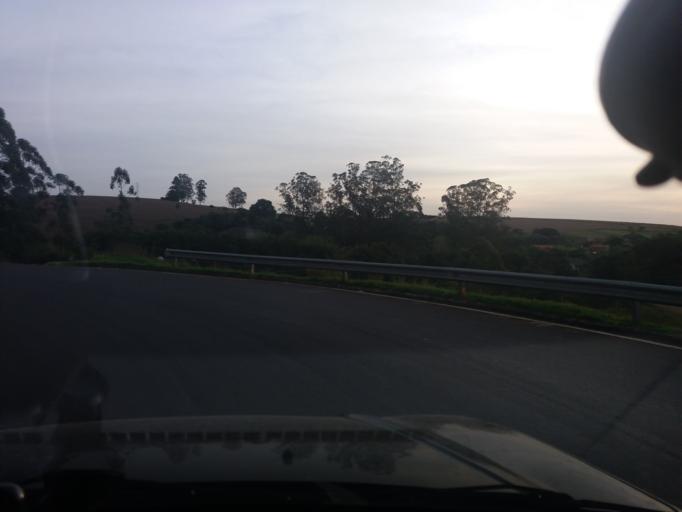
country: BR
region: Sao Paulo
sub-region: Itapetininga
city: Itapetininga
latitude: -23.7668
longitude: -48.1338
